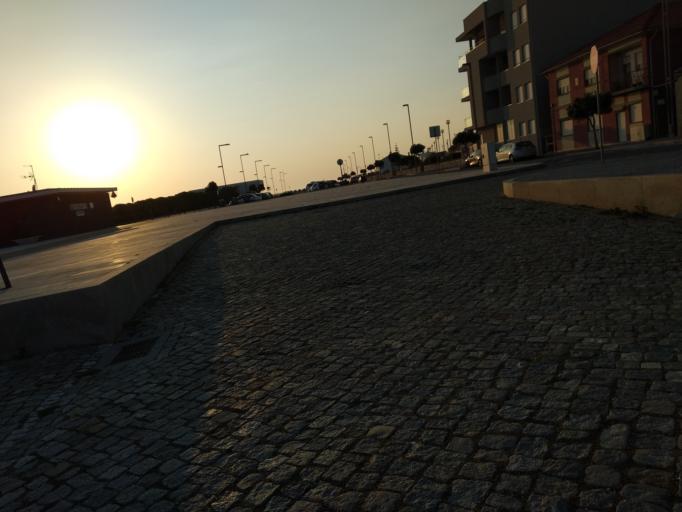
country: PT
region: Viana do Castelo
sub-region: Caminha
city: Vila Praia de Ancora
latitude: 41.8163
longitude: -8.8680
